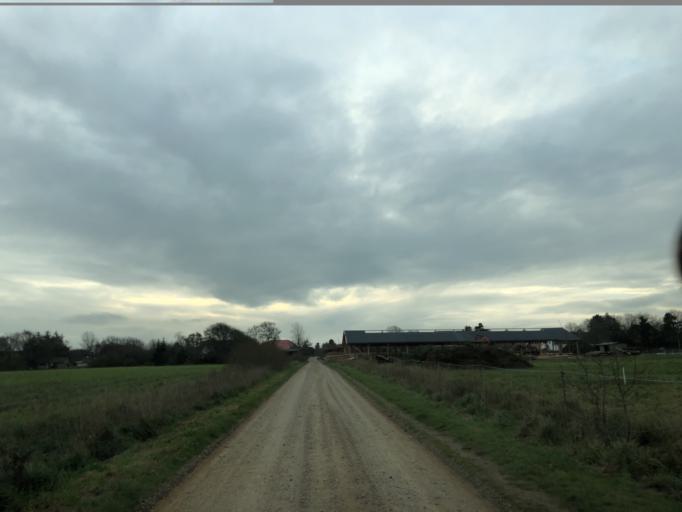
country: DK
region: Central Jutland
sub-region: Holstebro Kommune
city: Ulfborg
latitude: 56.2827
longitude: 8.1812
